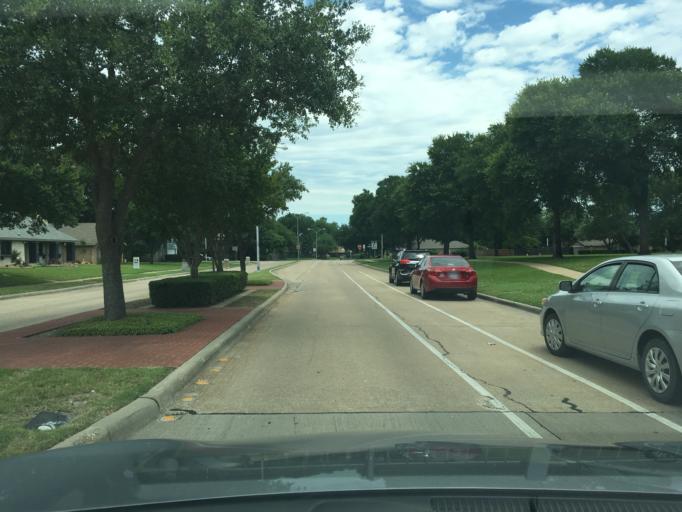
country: US
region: Texas
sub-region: Dallas County
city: Richardson
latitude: 32.9667
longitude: -96.6923
